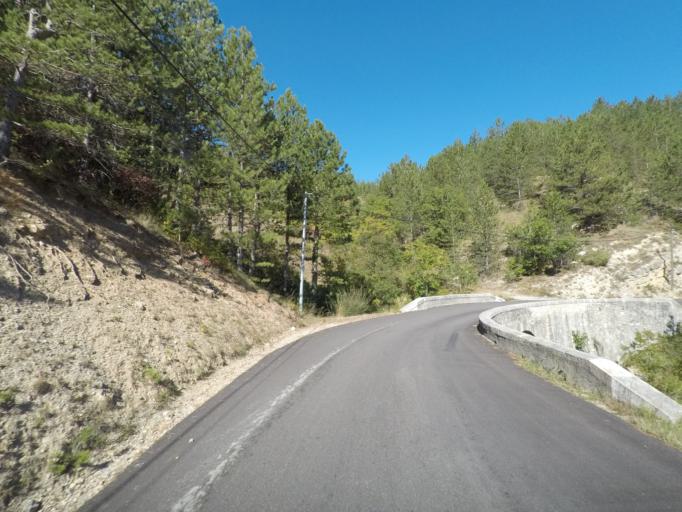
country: FR
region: Rhone-Alpes
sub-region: Departement de la Drome
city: Die
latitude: 44.6686
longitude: 5.2684
